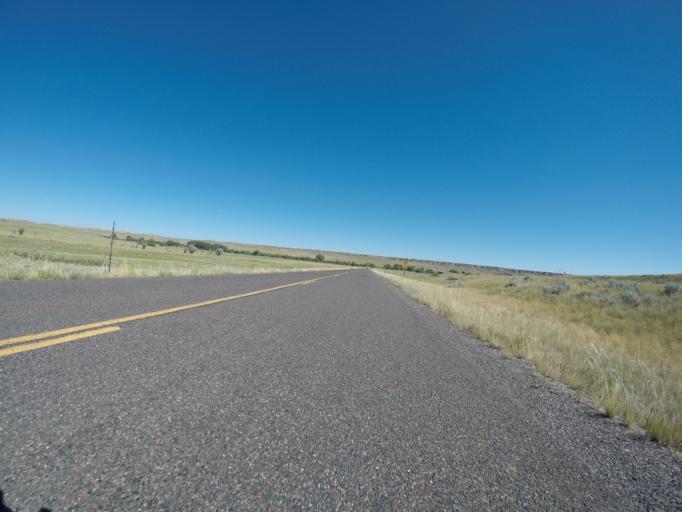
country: US
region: Wyoming
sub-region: Platte County
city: Wheatland
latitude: 41.7422
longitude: -104.8318
